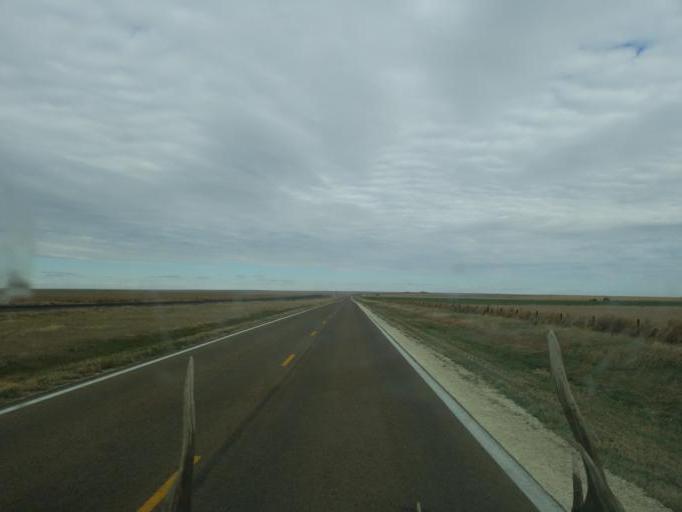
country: US
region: Kansas
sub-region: Wallace County
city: Sharon Springs
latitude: 38.9877
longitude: -101.4169
